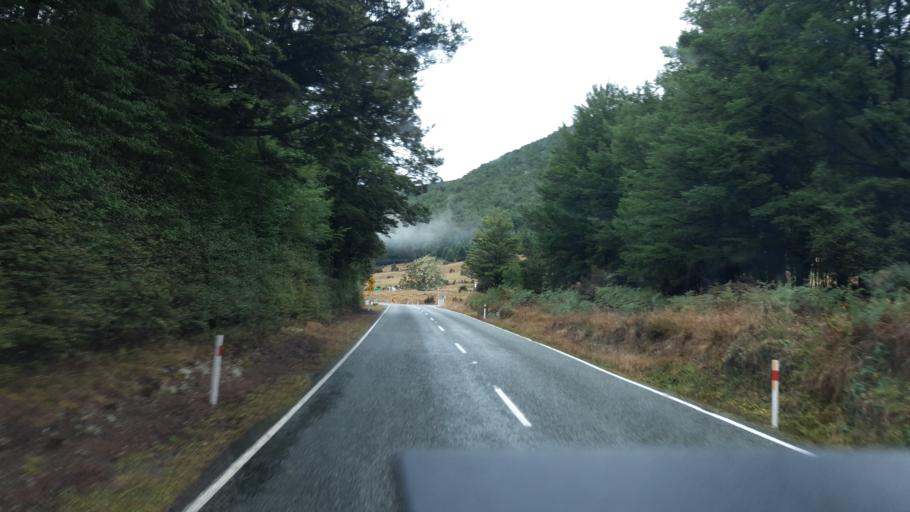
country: NZ
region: Tasman
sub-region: Tasman District
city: Wakefield
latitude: -41.7597
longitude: 172.8987
